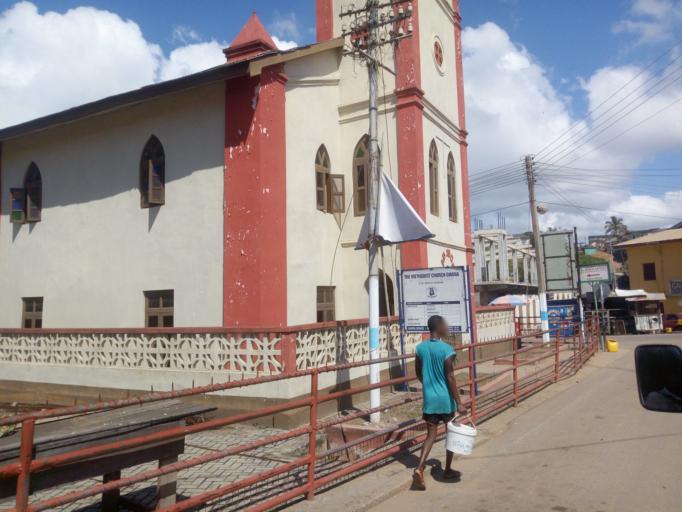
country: GH
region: Central
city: Elmina
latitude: 5.0855
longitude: -1.3497
